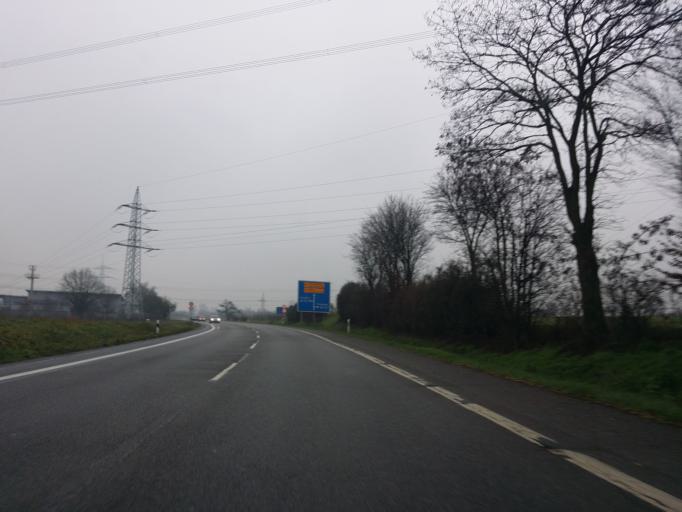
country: DE
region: Hesse
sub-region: Regierungsbezirk Darmstadt
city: Hofheim am Taunus
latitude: 50.0613
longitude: 8.4333
